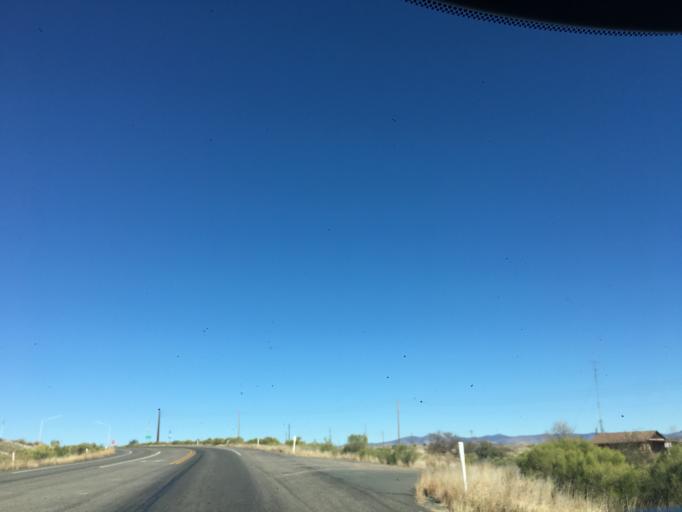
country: US
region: Arizona
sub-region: Yavapai County
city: Cordes Lakes
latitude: 34.3312
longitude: -112.1176
